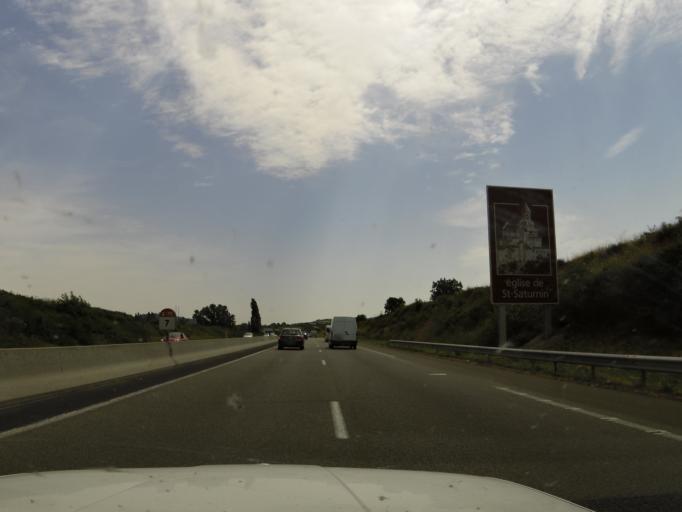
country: FR
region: Auvergne
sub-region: Departement du Puy-de-Dome
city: Orcet
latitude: 45.7150
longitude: 3.1517
